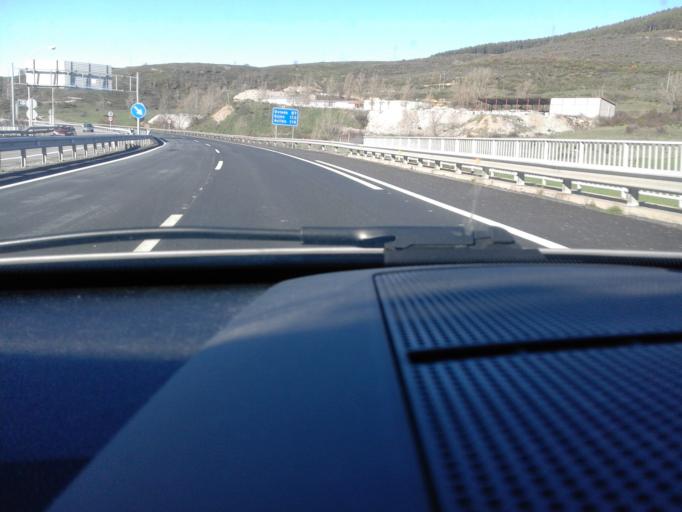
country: ES
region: Castille and Leon
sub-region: Provincia de Leon
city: Carrocera
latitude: 42.7842
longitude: -5.7878
